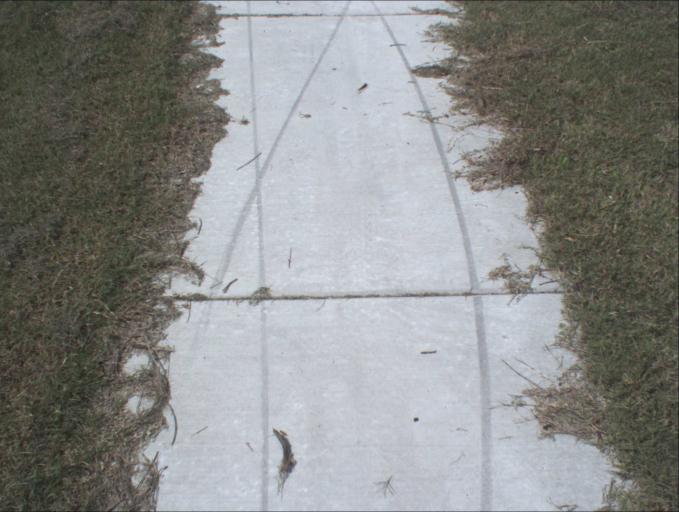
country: AU
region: Queensland
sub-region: Logan
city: Park Ridge South
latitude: -27.6928
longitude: 153.0115
